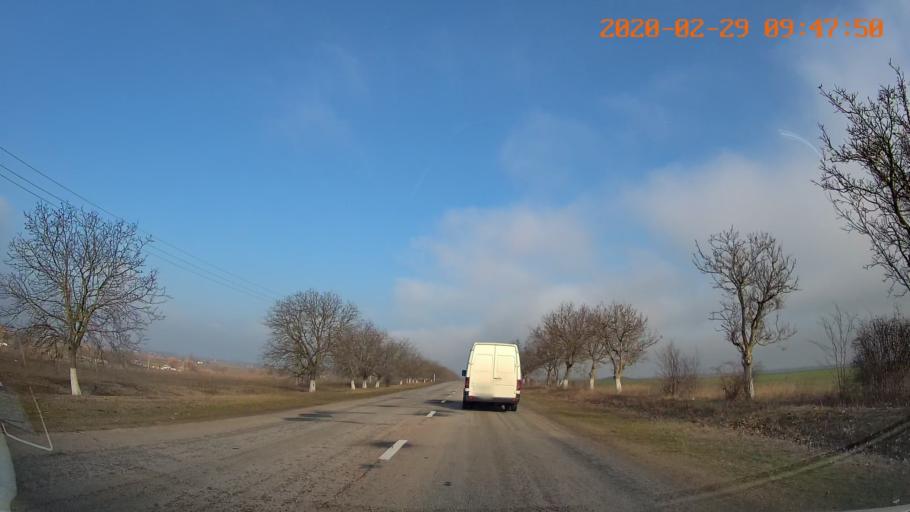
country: MD
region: Telenesti
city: Crasnoe
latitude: 46.6810
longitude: 29.7879
